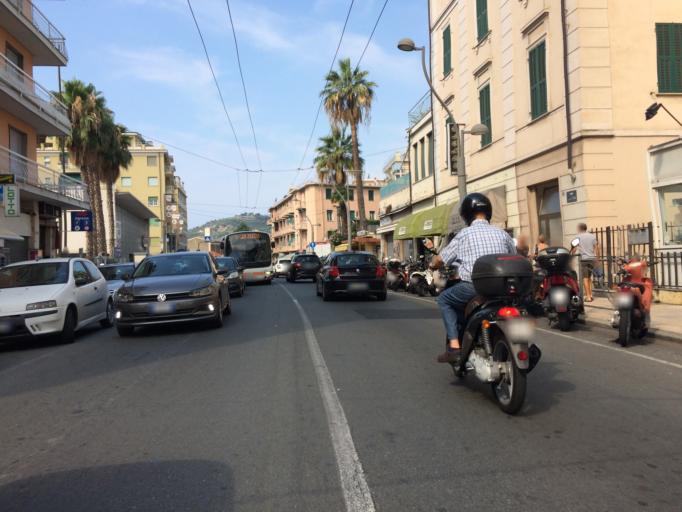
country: IT
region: Liguria
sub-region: Provincia di Imperia
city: San Remo
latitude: 43.8108
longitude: 7.7607
